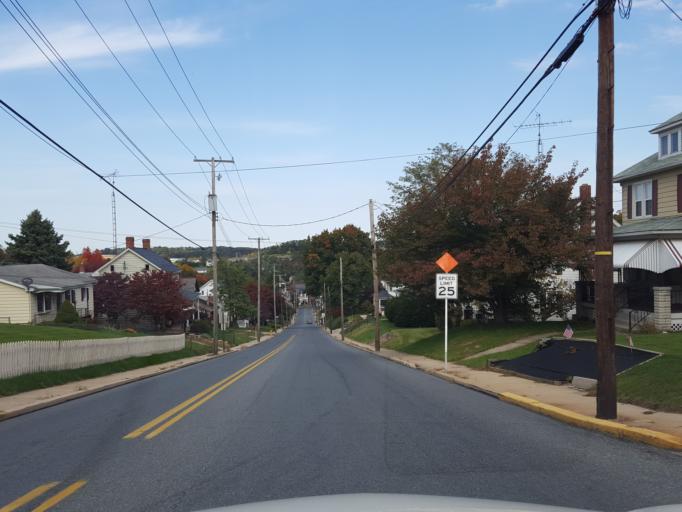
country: US
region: Pennsylvania
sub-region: York County
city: Yoe
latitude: 39.9051
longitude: -76.6374
